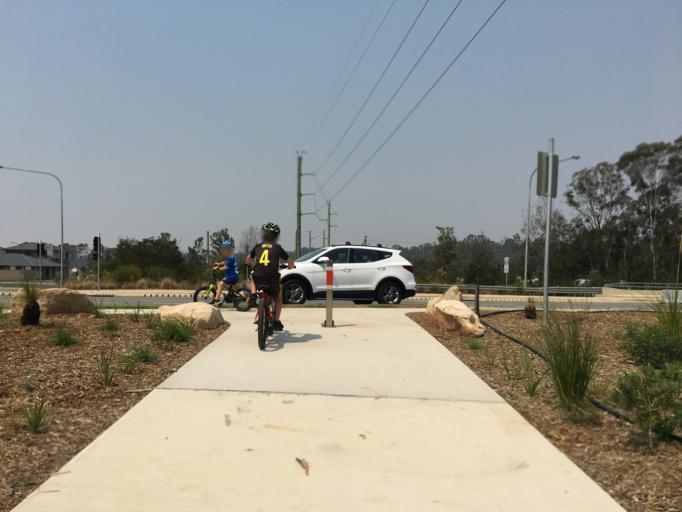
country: AU
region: New South Wales
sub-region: Campbelltown Municipality
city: Denham Court
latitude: -33.9720
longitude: 150.8168
